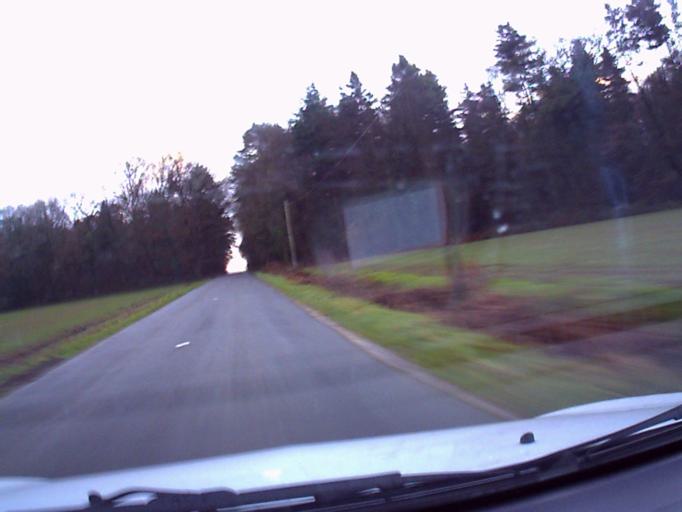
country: FR
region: Brittany
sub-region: Departement d'Ille-et-Vilaine
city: Iffendic
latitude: 48.1578
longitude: -2.0137
